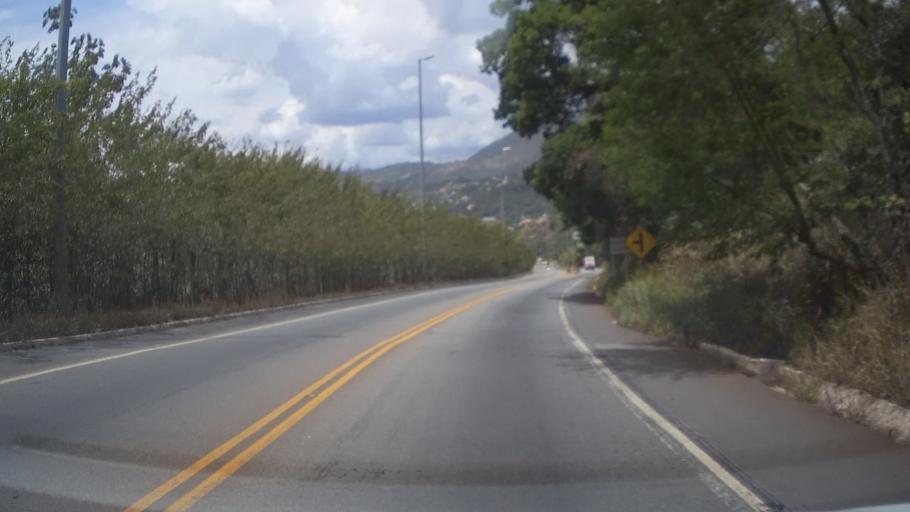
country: BR
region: Minas Gerais
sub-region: Nova Lima
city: Nova Lima
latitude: -19.9931
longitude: -43.8578
